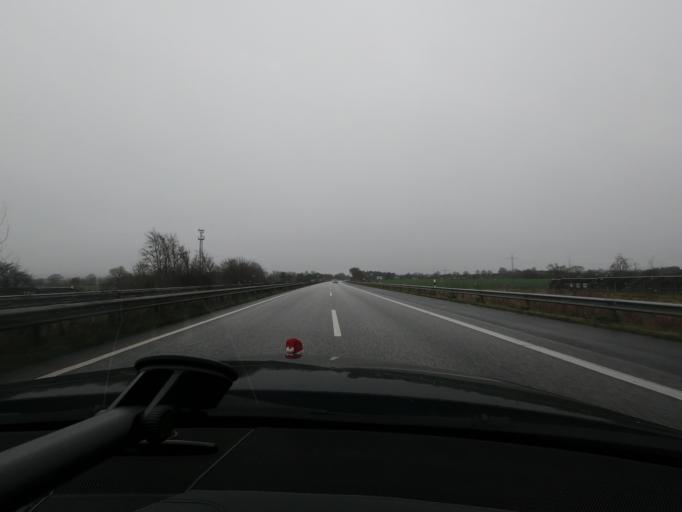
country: DE
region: Schleswig-Holstein
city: Lurschau
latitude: 54.5835
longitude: 9.4660
